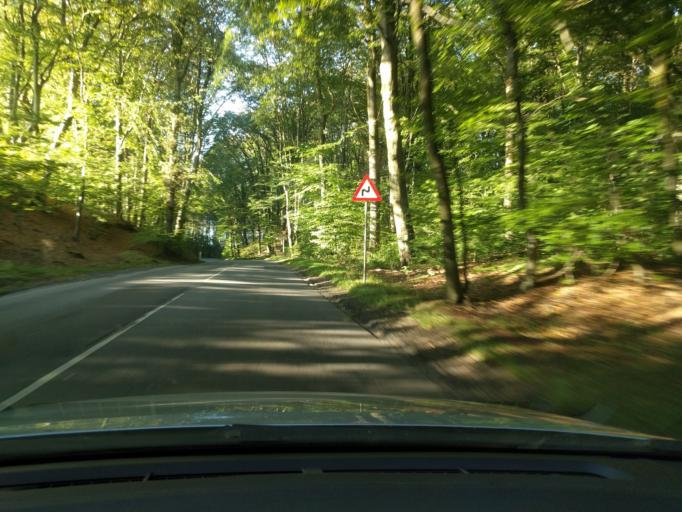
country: DK
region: Central Jutland
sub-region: Skanderborg Kommune
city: Ry
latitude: 56.0948
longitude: 9.7820
